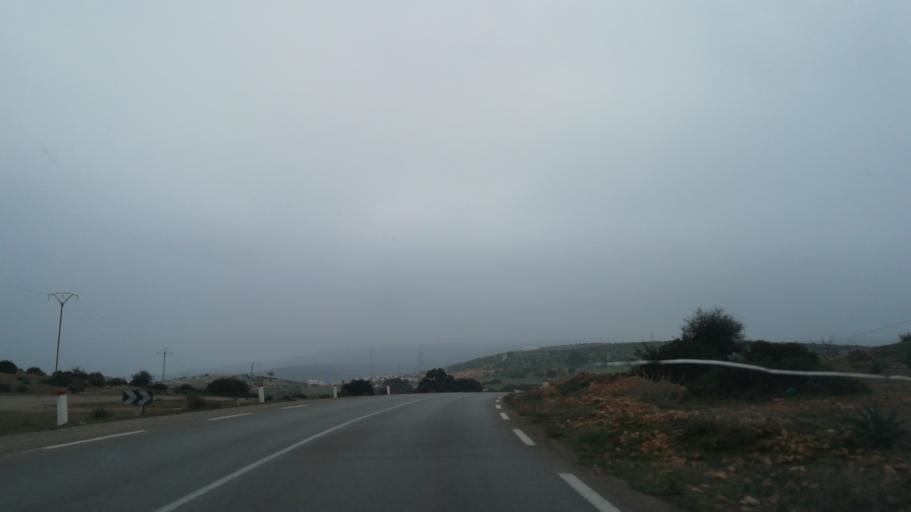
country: DZ
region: Mascara
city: Oued el Abtal
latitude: 35.2941
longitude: 0.4635
